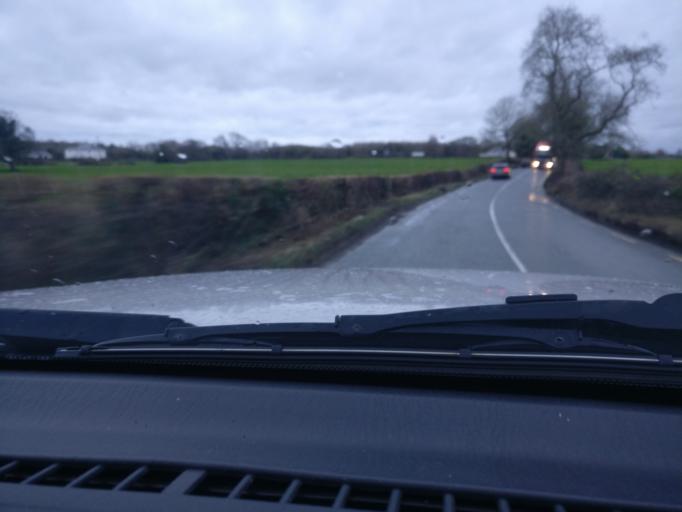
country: IE
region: Leinster
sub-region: An Mhi
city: Longwood
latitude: 53.4951
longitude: -6.8595
